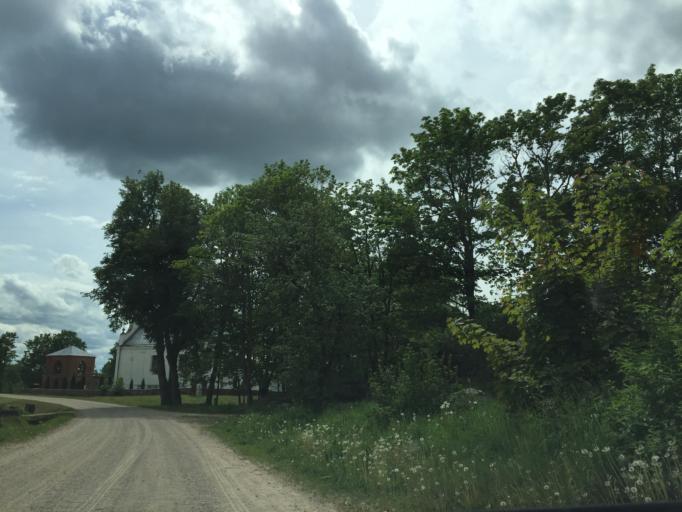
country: LV
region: Dagda
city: Dagda
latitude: 56.0286
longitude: 27.6219
